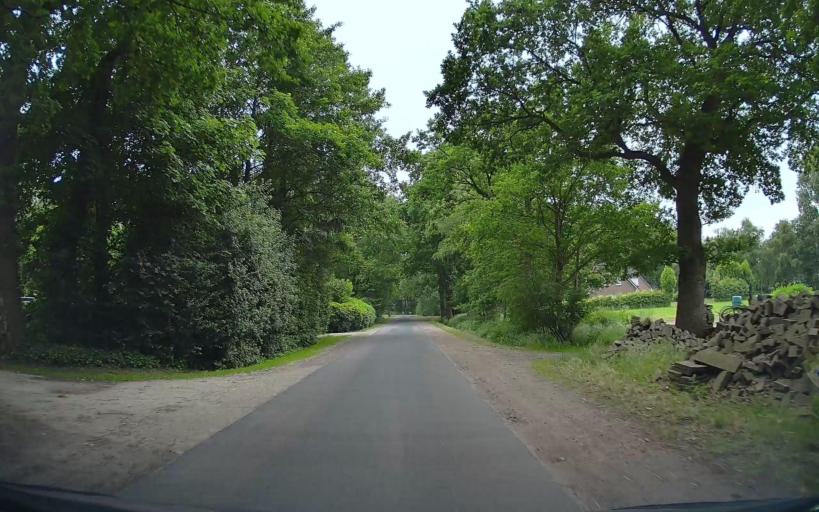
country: DE
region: Lower Saxony
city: Friesoythe
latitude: 53.0264
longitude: 7.9027
